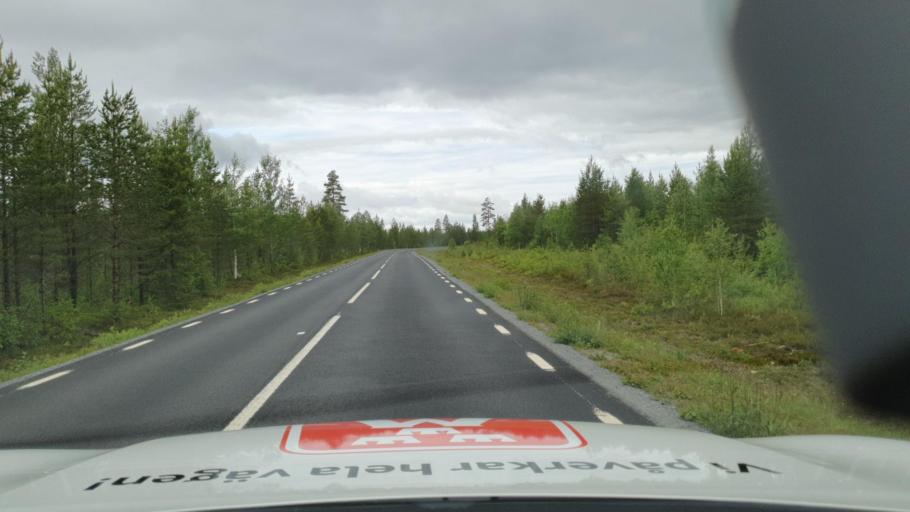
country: SE
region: Vaesterbotten
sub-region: Dorotea Kommun
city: Dorotea
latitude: 64.1905
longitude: 16.5993
